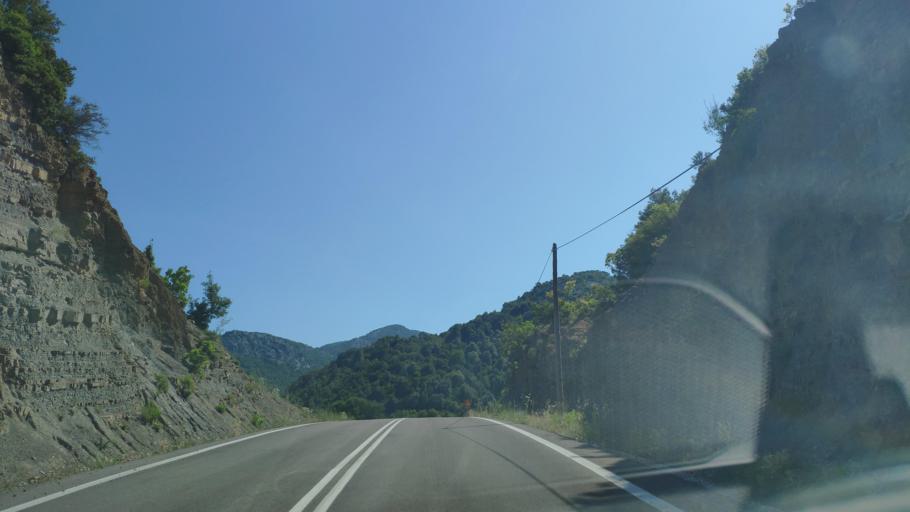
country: GR
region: West Greece
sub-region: Nomos Aitolias kai Akarnanias
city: Sardinia
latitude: 38.9249
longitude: 21.4140
